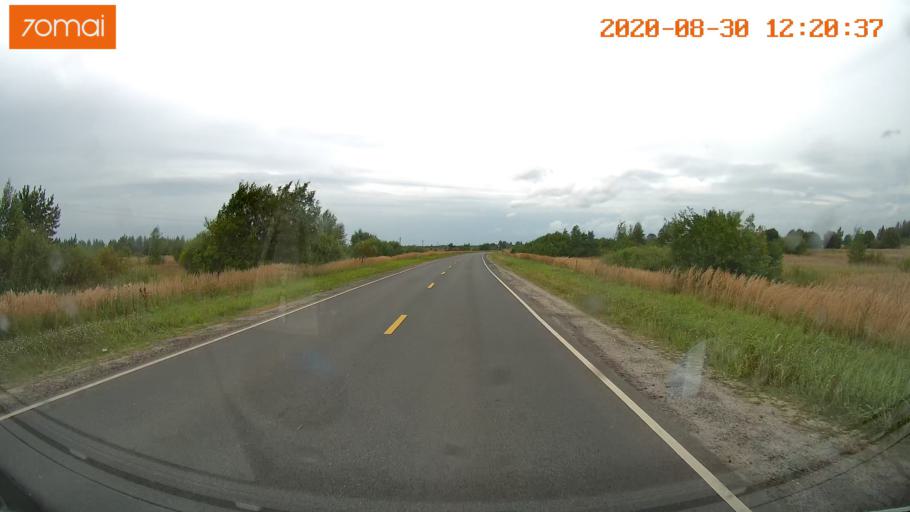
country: RU
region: Ivanovo
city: Yur'yevets
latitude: 57.3228
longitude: 42.8971
